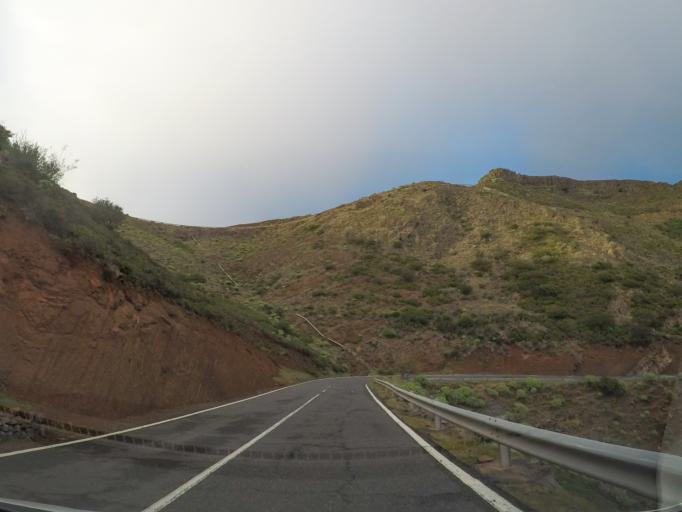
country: ES
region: Canary Islands
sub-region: Provincia de Santa Cruz de Tenerife
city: Alajero
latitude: 28.0883
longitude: -17.2543
